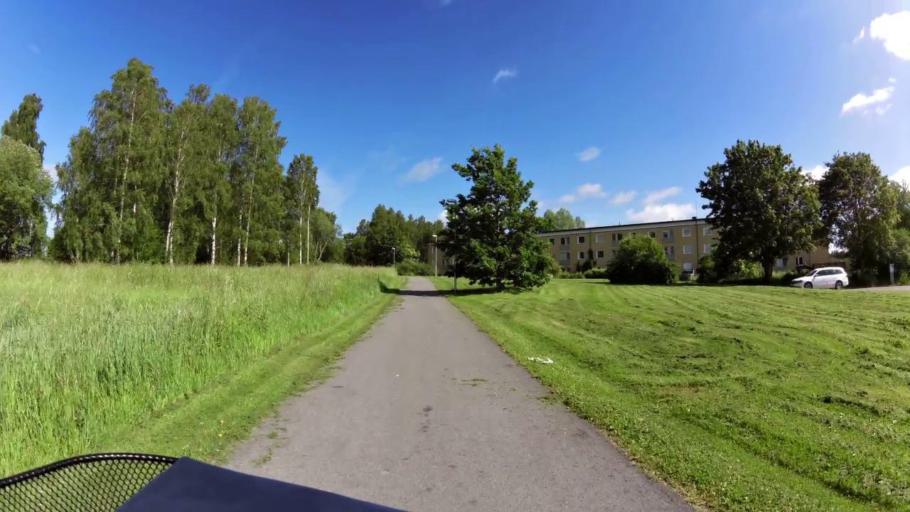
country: SE
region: OEstergoetland
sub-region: Linkopings Kommun
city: Linkoping
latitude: 58.3866
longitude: 15.6365
